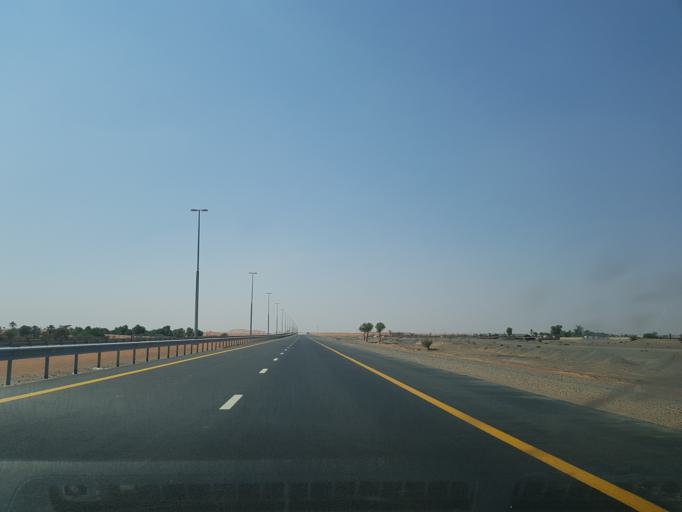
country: AE
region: Ash Shariqah
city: Adh Dhayd
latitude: 25.2369
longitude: 55.8991
